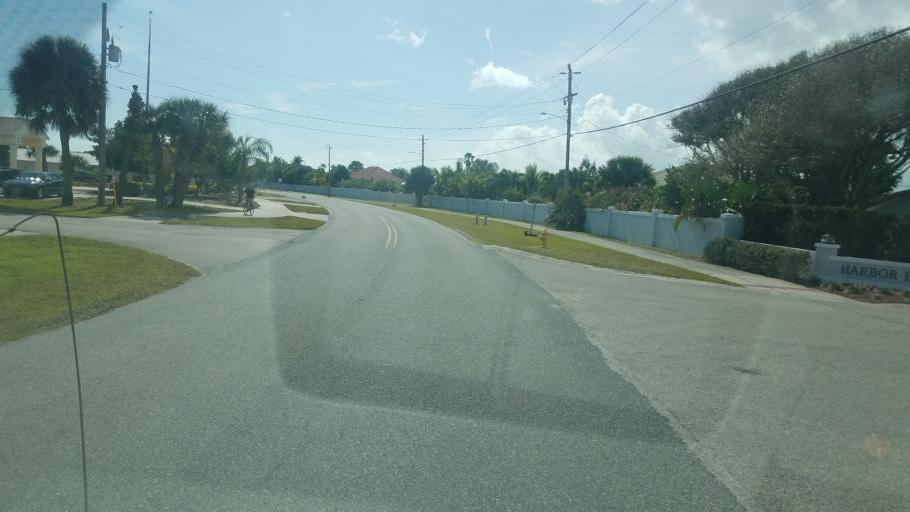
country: US
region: Florida
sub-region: Brevard County
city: Melbourne Beach
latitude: 28.0605
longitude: -80.5608
